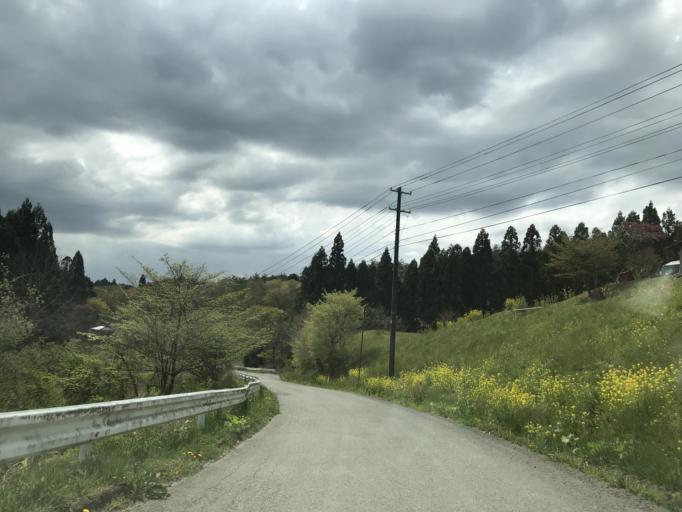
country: JP
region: Iwate
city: Ichinoseki
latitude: 38.7872
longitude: 141.4284
